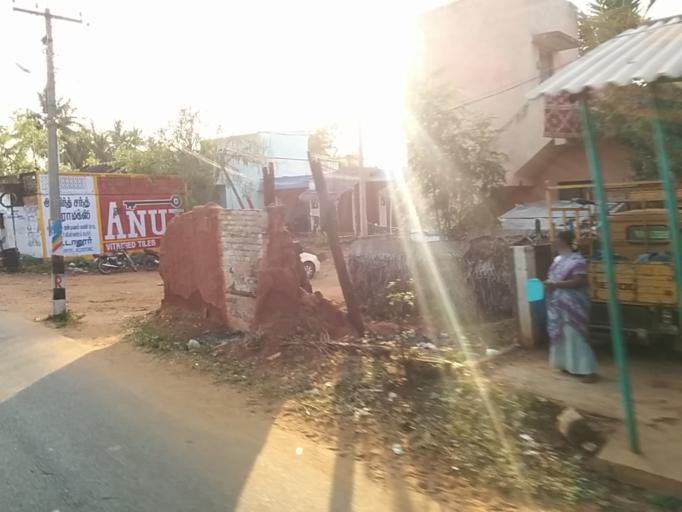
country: IN
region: Tamil Nadu
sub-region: Villupuram
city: Auroville
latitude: 11.9939
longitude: 79.8509
